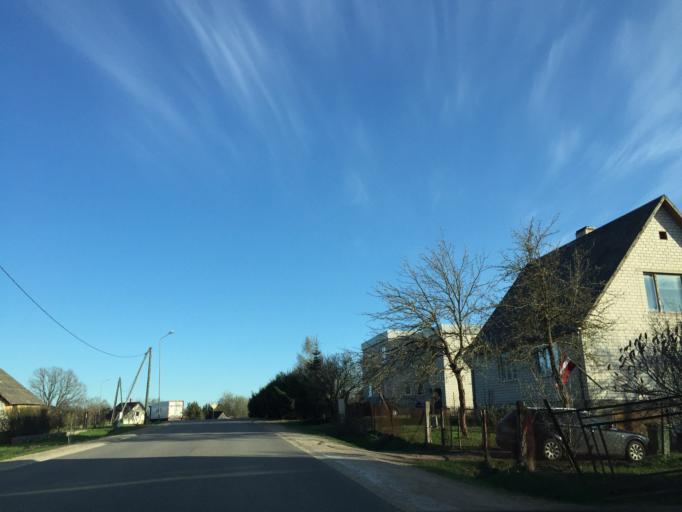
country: LV
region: Valkas Rajons
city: Valka
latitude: 57.7685
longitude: 26.0009
